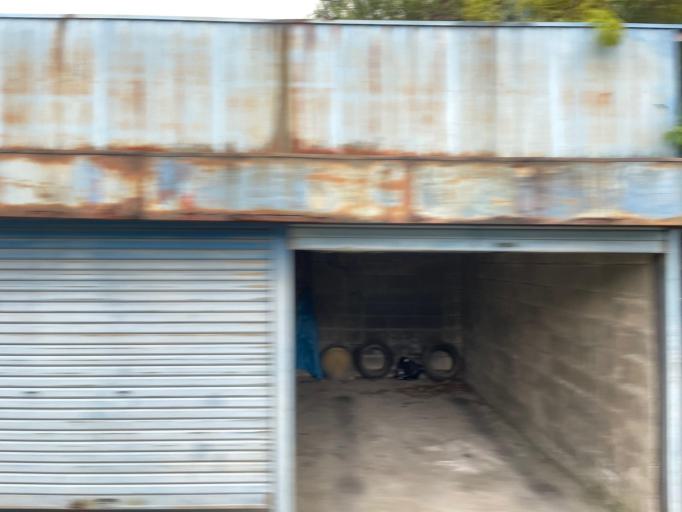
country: JP
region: Tochigi
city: Tanuma
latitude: 36.4708
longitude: 139.6295
